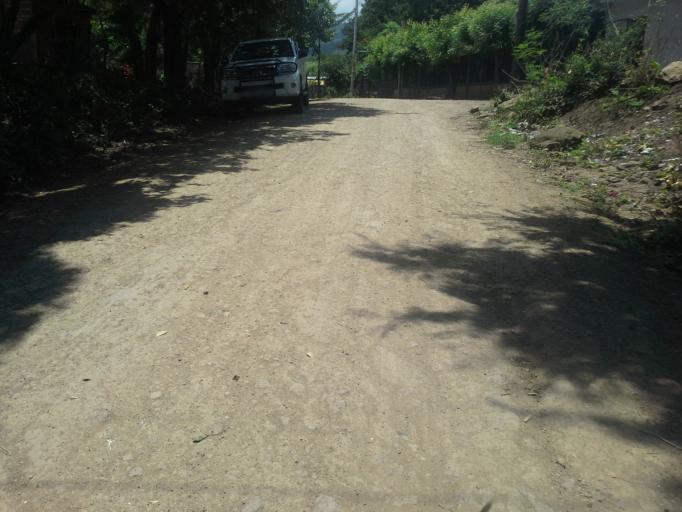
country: NI
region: Matagalpa
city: Ciudad Dario
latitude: 12.6994
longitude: -86.0523
